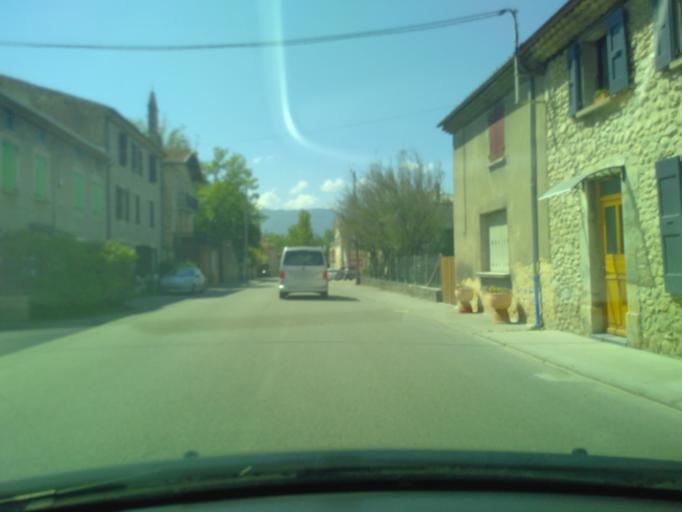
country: FR
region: Rhone-Alpes
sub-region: Departement de la Drome
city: Die
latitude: 44.7095
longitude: 5.4016
